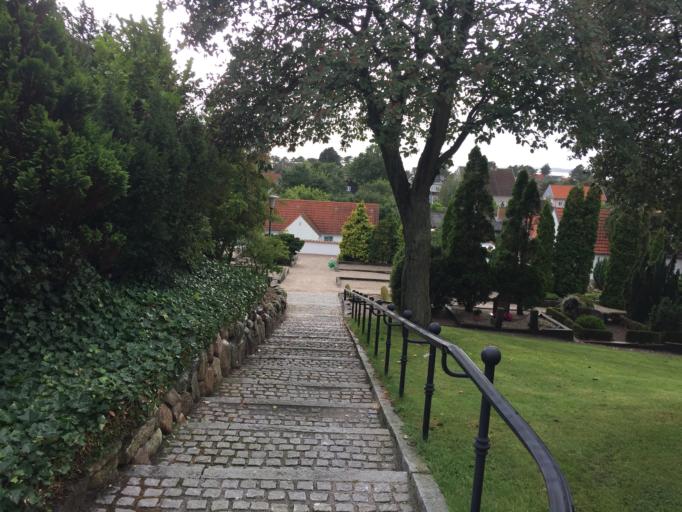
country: DK
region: Capital Region
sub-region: Halsnaes Kommune
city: Hundested
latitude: 55.9511
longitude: 11.8593
